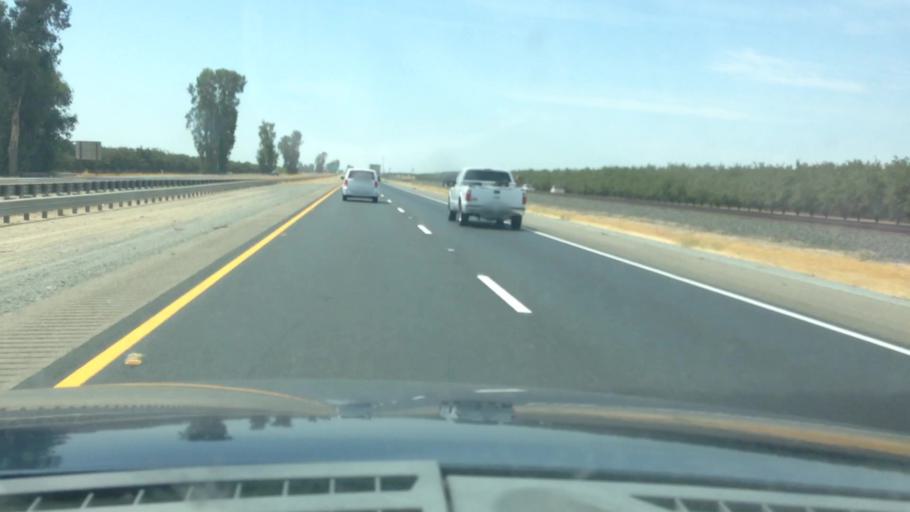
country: US
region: California
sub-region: Tulare County
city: Earlimart
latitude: 35.8617
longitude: -119.2691
